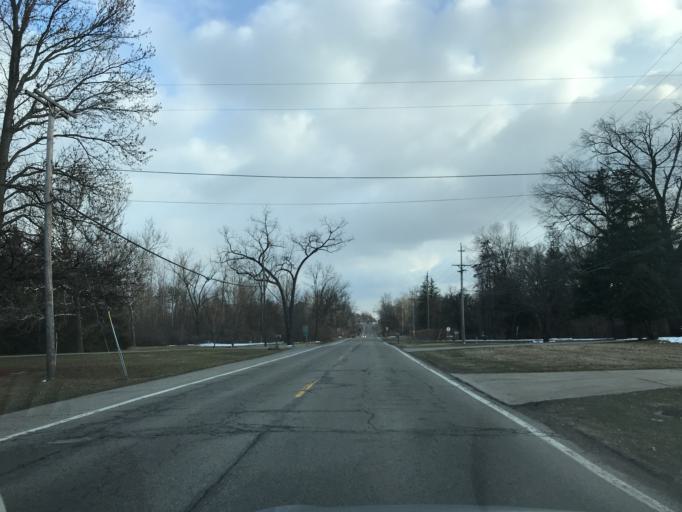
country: US
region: Michigan
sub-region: Wayne County
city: Redford
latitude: 42.4511
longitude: -83.2979
